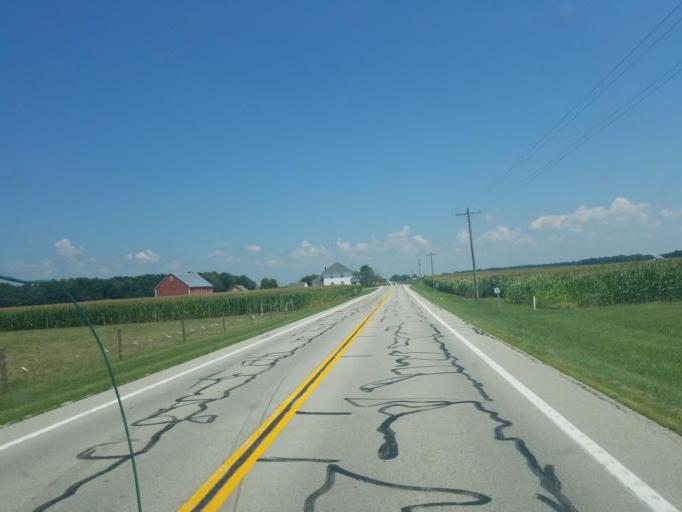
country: US
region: Ohio
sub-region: Shelby County
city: Anna
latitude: 40.3953
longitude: -84.1312
